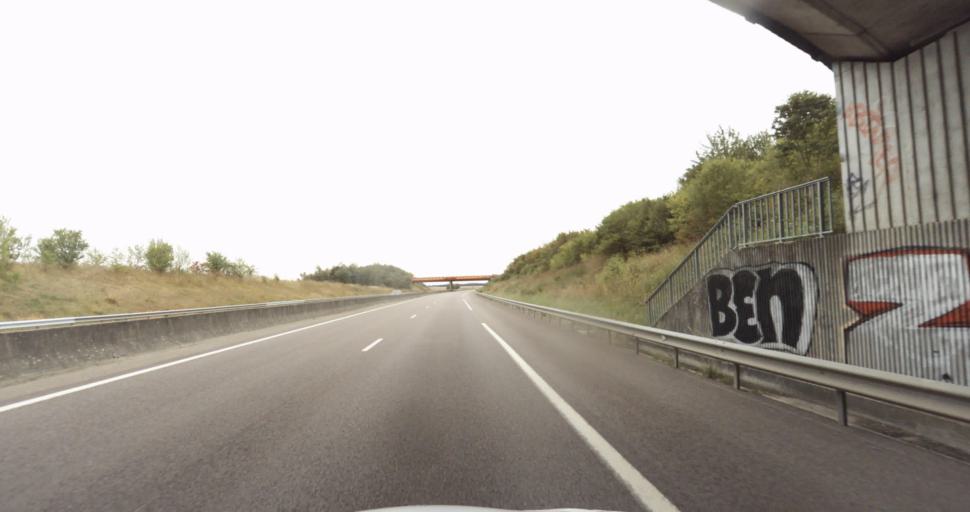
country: FR
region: Haute-Normandie
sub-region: Departement de l'Eure
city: Evreux
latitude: 48.9275
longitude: 1.2057
